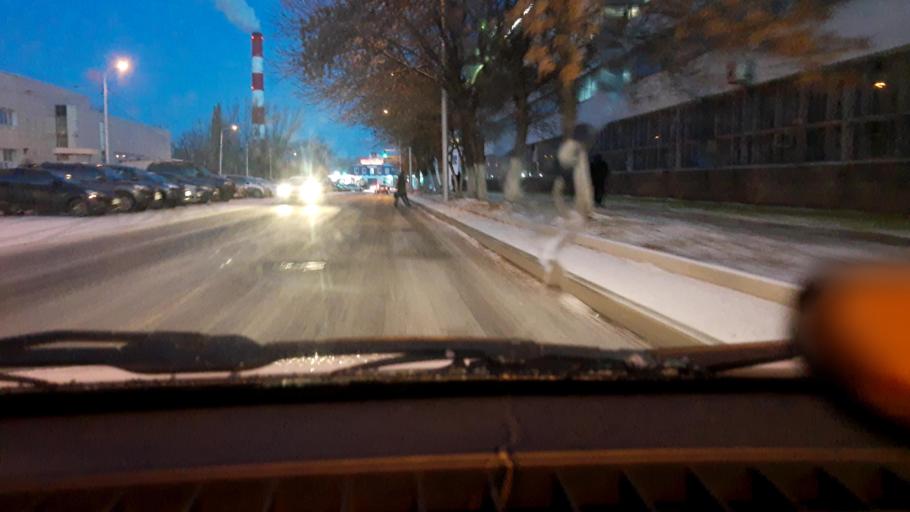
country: RU
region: Bashkortostan
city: Ufa
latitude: 54.7398
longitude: 55.9818
